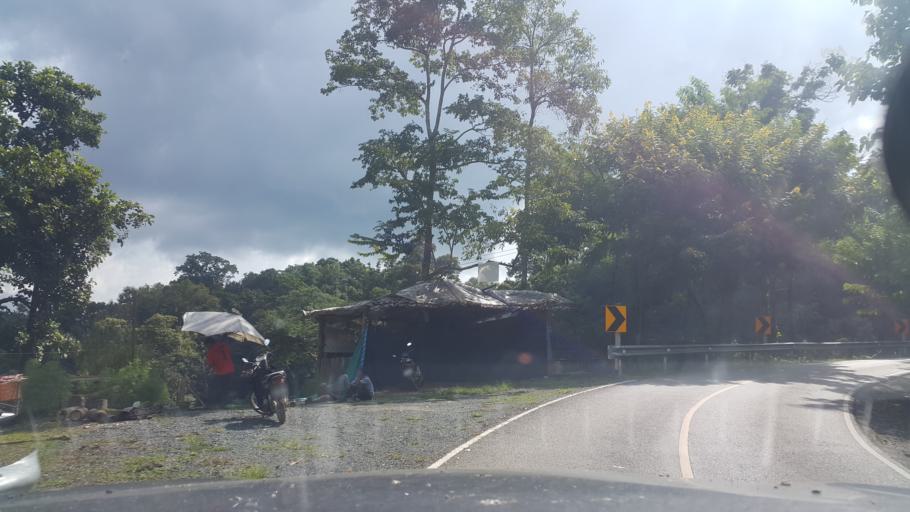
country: TH
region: Chiang Mai
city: Mae On
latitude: 18.8626
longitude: 99.2919
